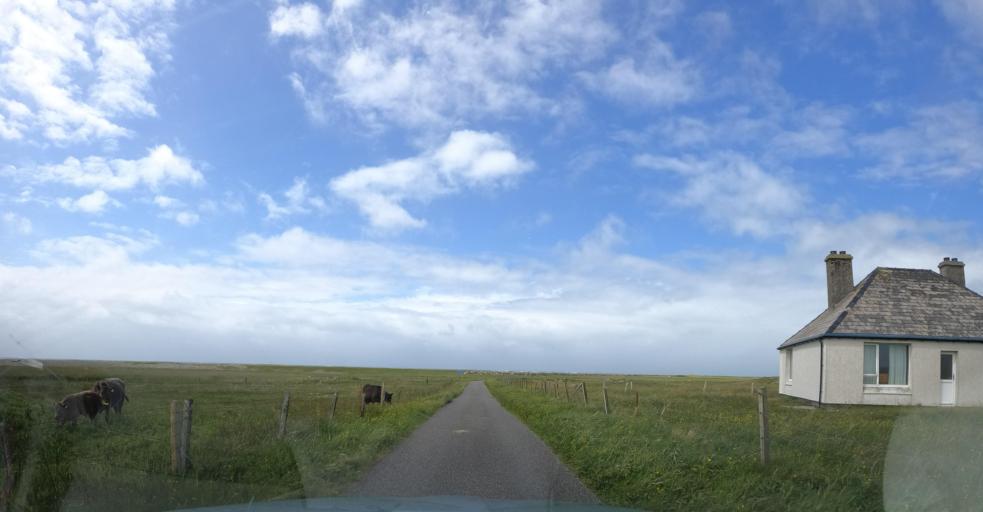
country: GB
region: Scotland
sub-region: Eilean Siar
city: Isle of South Uist
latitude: 57.2796
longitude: -7.4158
